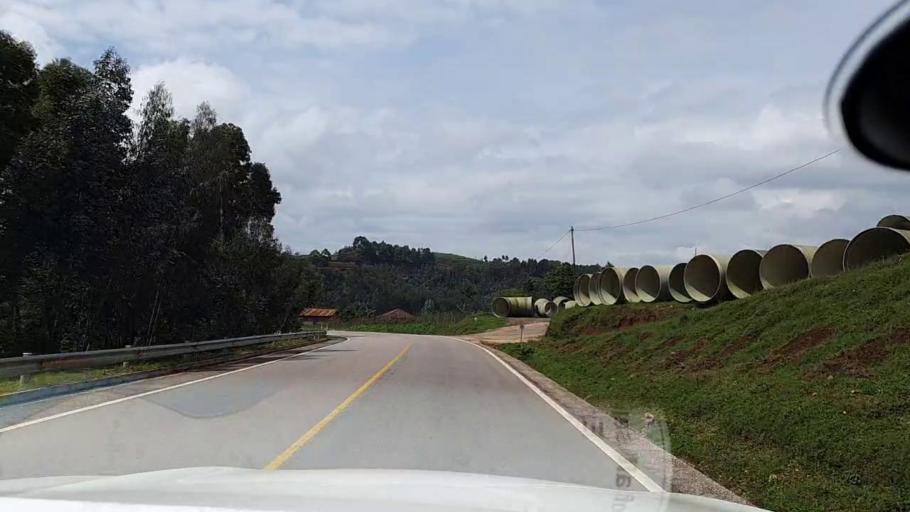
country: RW
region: Southern Province
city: Nzega
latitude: -2.4884
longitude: 29.5122
